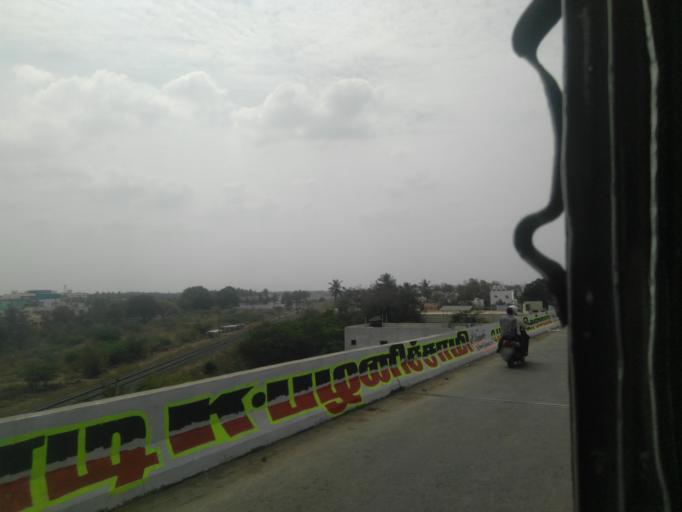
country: IN
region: Tamil Nadu
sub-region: Coimbatore
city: Irugur
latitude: 11.0023
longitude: 77.0540
